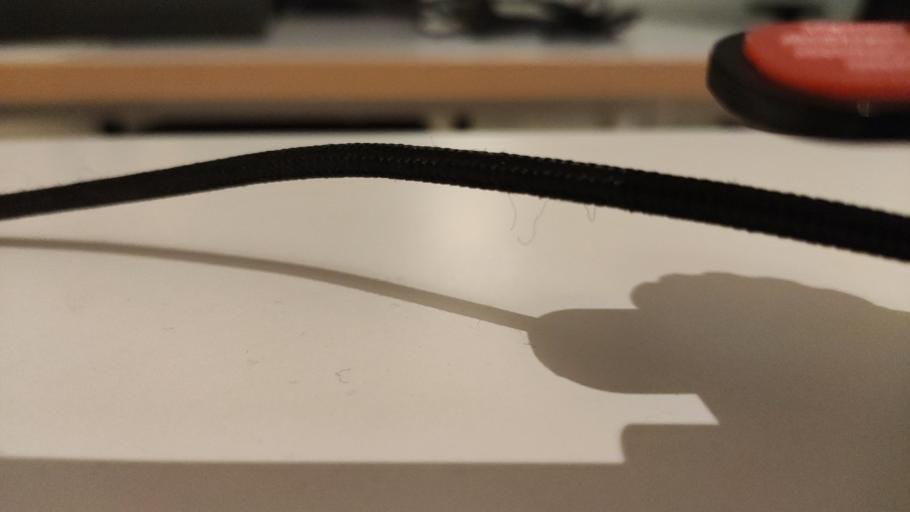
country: RU
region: Moskovskaya
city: Semkhoz
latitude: 56.3842
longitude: 38.0647
